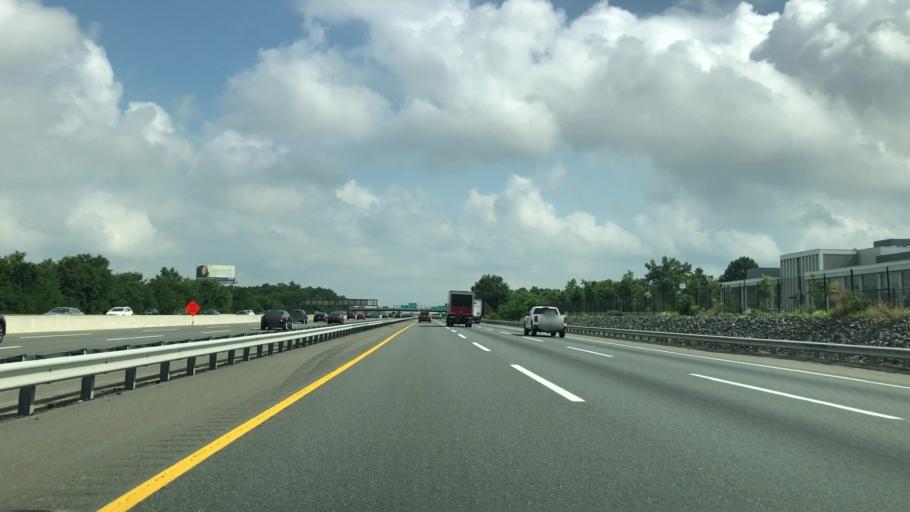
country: US
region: New Jersey
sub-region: Middlesex County
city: Rossmoor
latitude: 40.3381
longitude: -74.4789
